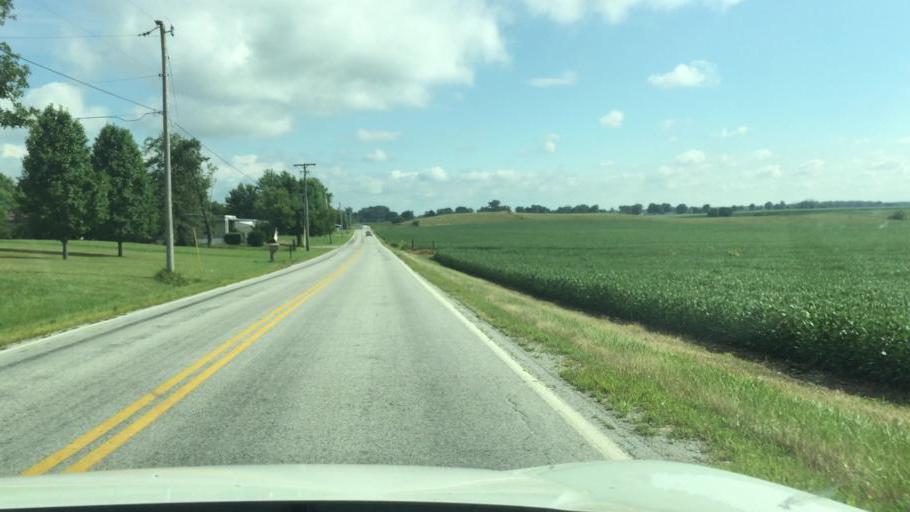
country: US
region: Ohio
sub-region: Clark County
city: Lisbon
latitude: 39.9534
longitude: -83.6808
